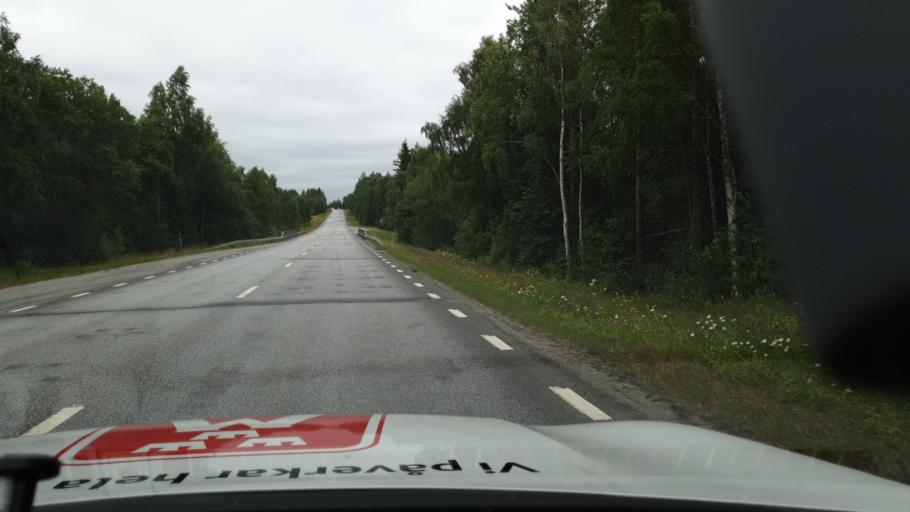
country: SE
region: Vaesterbotten
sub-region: Umea Kommun
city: Ersmark
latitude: 63.8875
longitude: 20.3085
